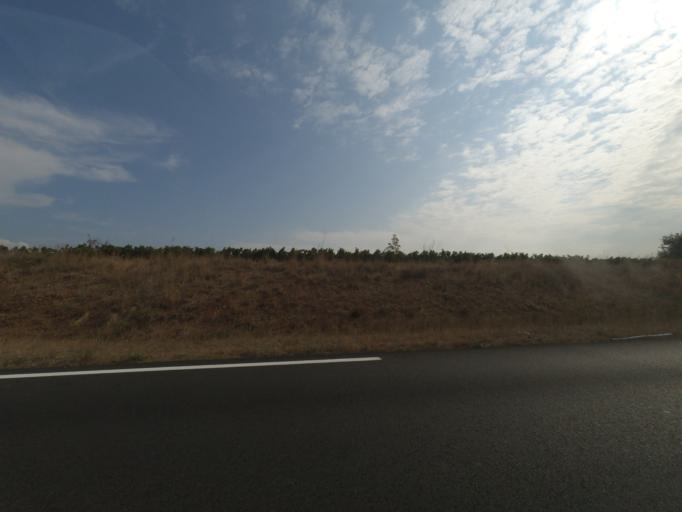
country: FR
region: Languedoc-Roussillon
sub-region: Departement de l'Herault
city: Saint-Christol
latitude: 43.7286
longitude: 4.0991
